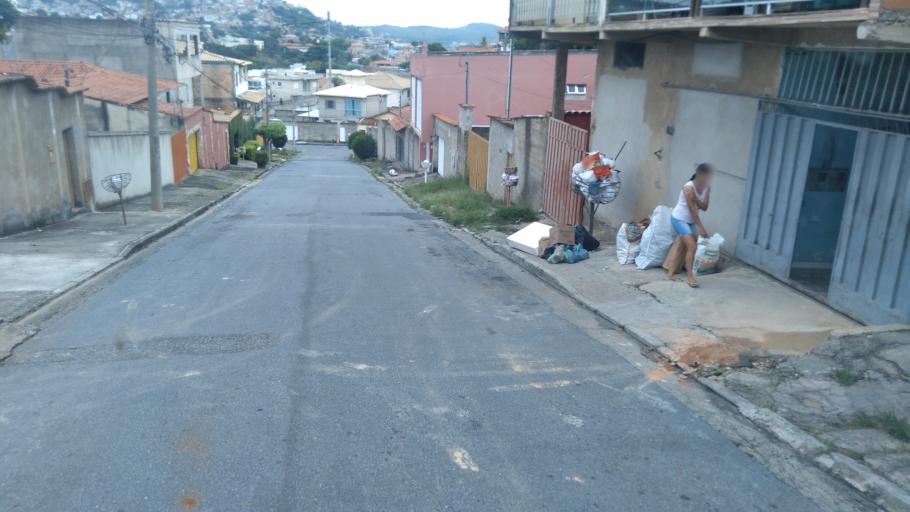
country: BR
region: Minas Gerais
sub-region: Belo Horizonte
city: Belo Horizonte
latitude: -19.8488
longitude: -43.9071
